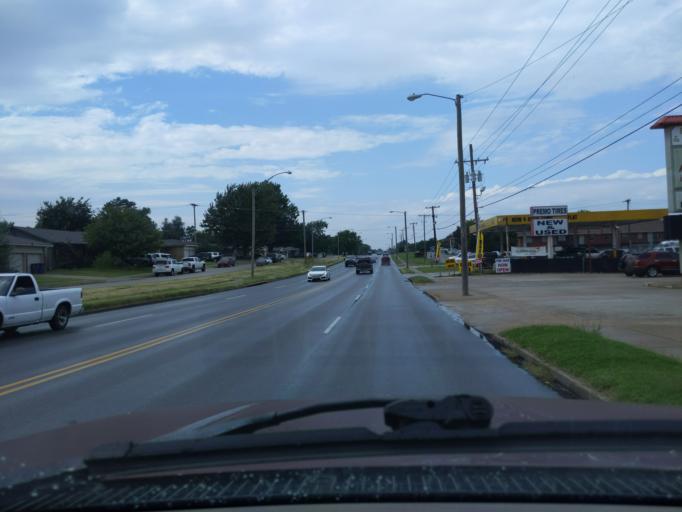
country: US
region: Oklahoma
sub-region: Tulsa County
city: Tulsa
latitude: 36.1335
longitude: -95.8899
